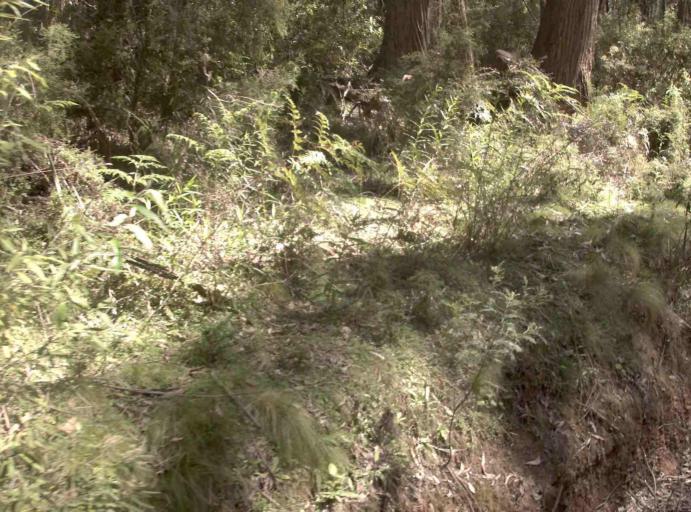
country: AU
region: New South Wales
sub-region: Bombala
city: Bombala
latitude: -37.0706
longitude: 148.7855
